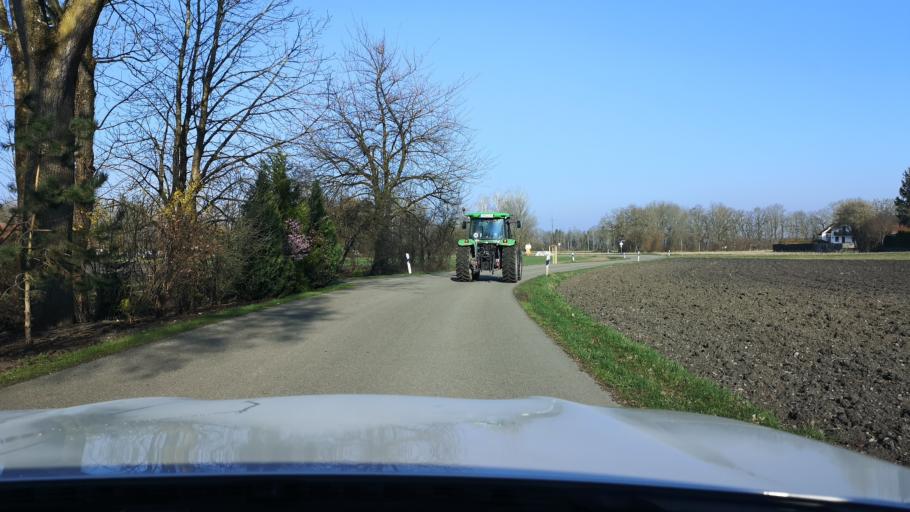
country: DE
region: Bavaria
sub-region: Upper Bavaria
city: Eichenried
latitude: 48.2443
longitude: 11.7772
